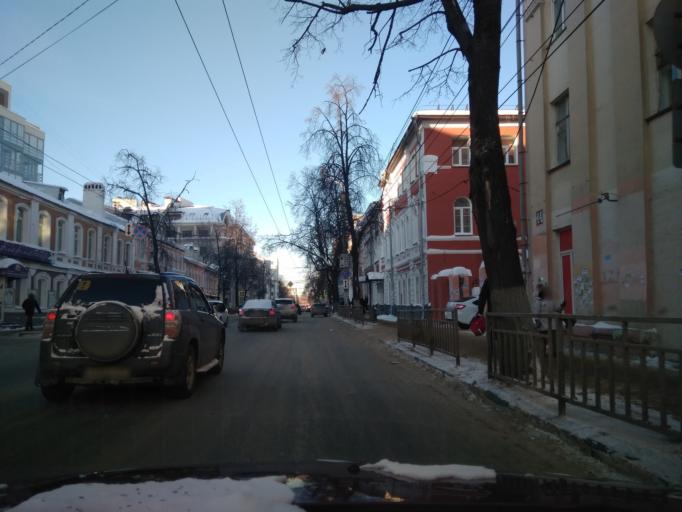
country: RU
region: Nizjnij Novgorod
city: Nizhniy Novgorod
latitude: 56.3192
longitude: 44.0148
